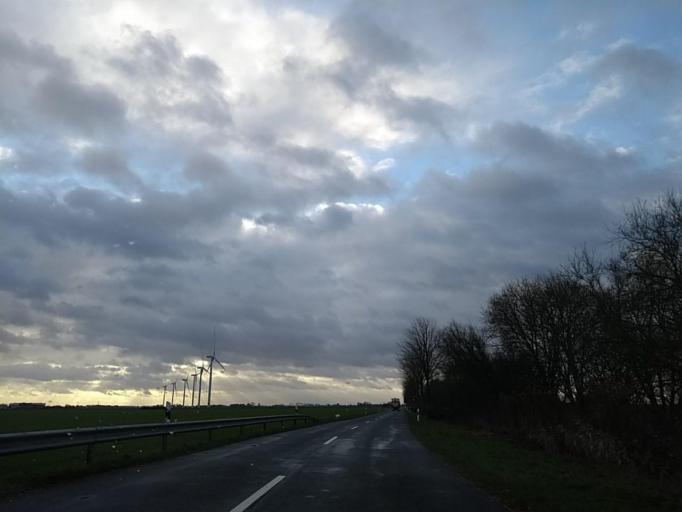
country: DE
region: Lower Saxony
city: Bunde
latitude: 53.2123
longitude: 7.2195
